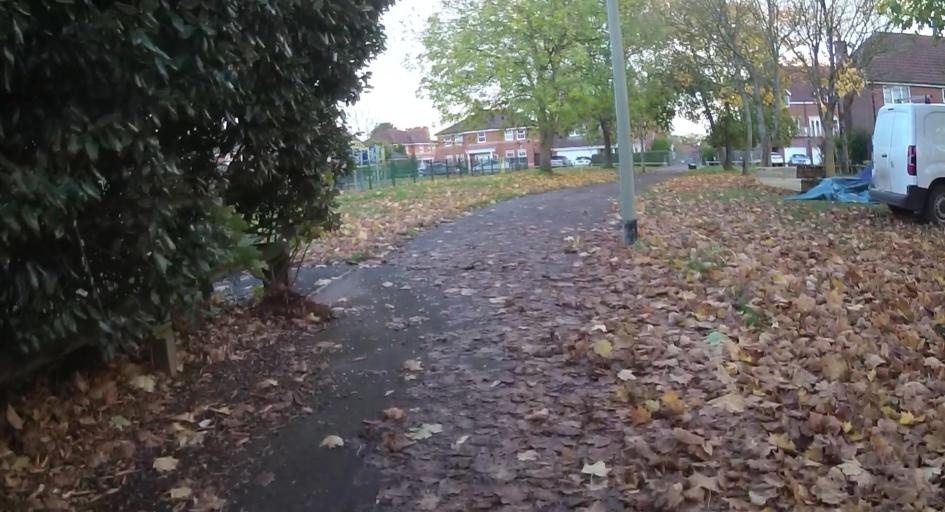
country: GB
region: England
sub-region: Wokingham
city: Shinfield
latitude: 51.4074
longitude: -0.9549
